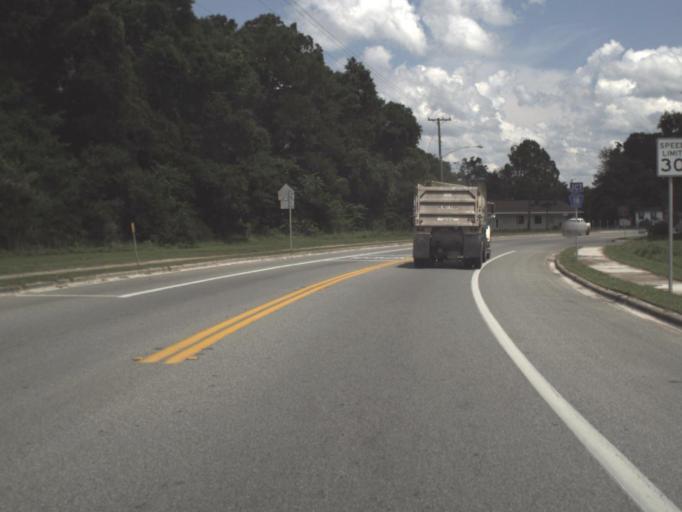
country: US
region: Florida
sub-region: Alachua County
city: High Springs
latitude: 29.9229
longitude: -82.7114
